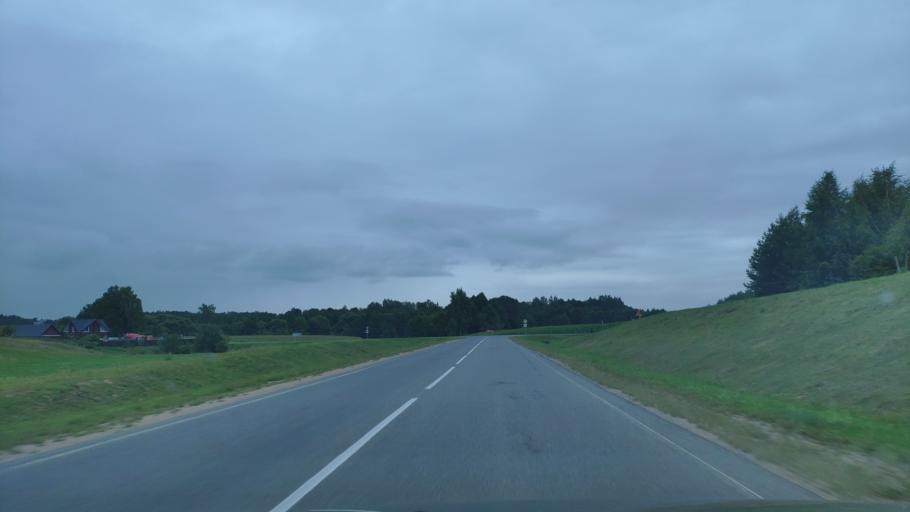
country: BY
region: Minsk
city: Azyartso
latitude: 53.8350
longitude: 27.3474
